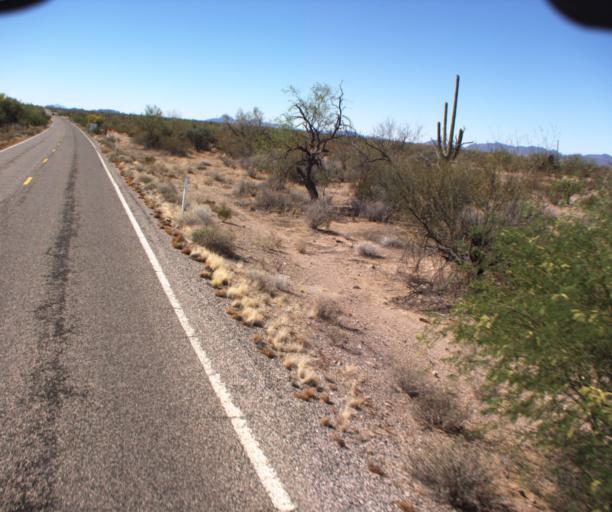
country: US
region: Arizona
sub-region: Pima County
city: Ajo
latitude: 32.2199
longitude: -112.7570
